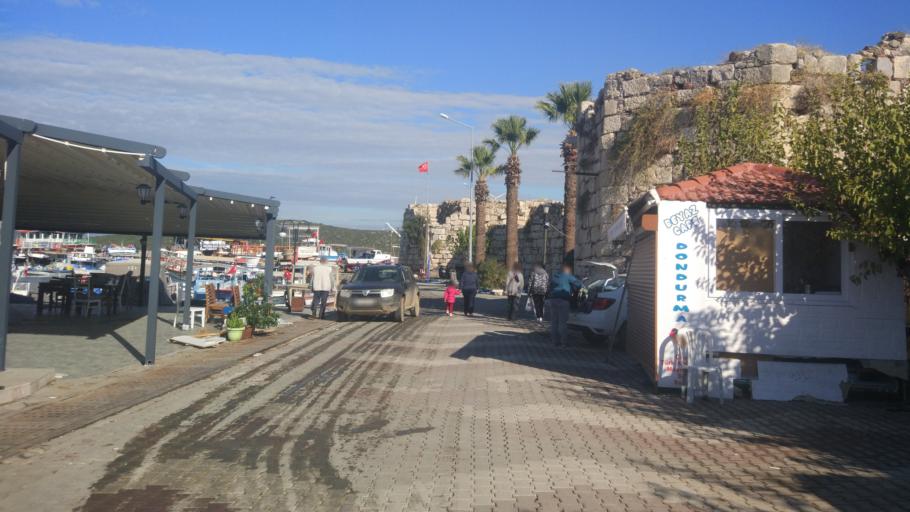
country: TR
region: Izmir
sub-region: Seferihisar
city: Seferhisar
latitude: 38.1941
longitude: 26.7843
